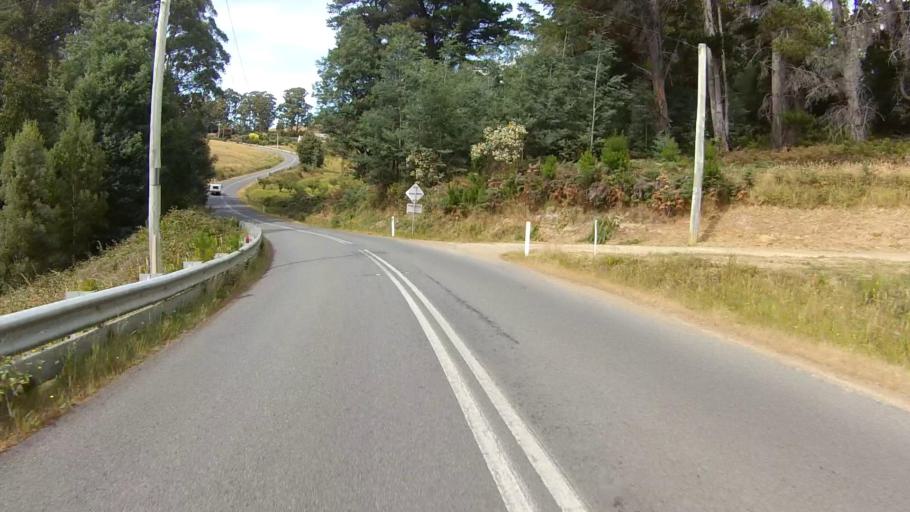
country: AU
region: Tasmania
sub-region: Kingborough
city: Kettering
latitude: -43.1972
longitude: 147.2507
